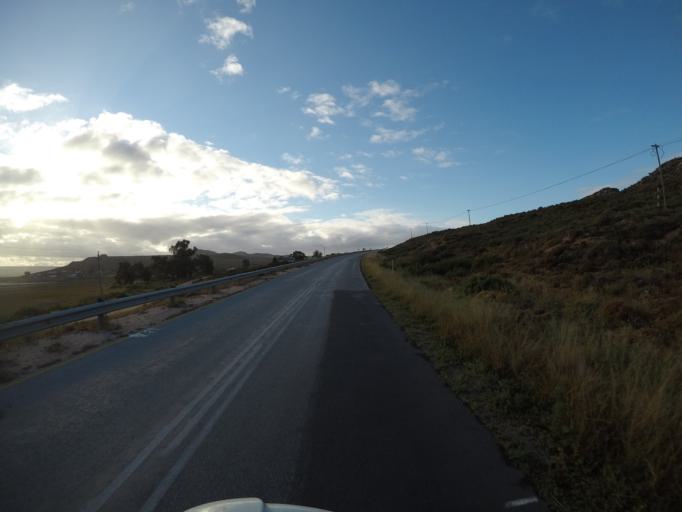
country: ZA
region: Western Cape
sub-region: West Coast District Municipality
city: Clanwilliam
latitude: -32.3270
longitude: 18.3685
